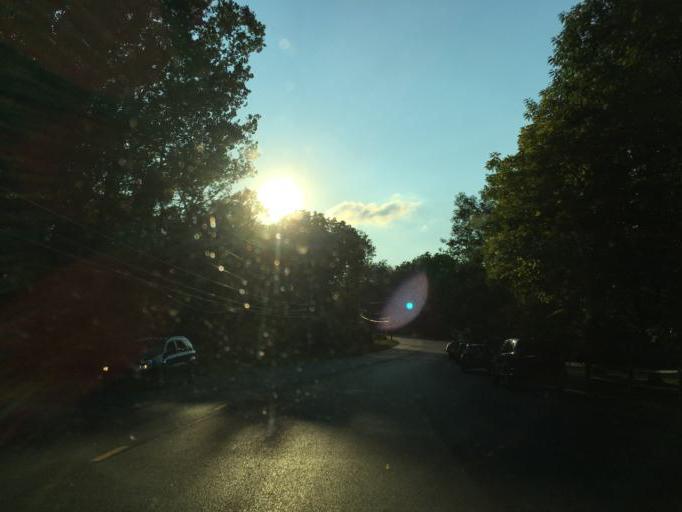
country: US
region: Maryland
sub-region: Baltimore County
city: Hampton
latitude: 39.4244
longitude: -76.5971
